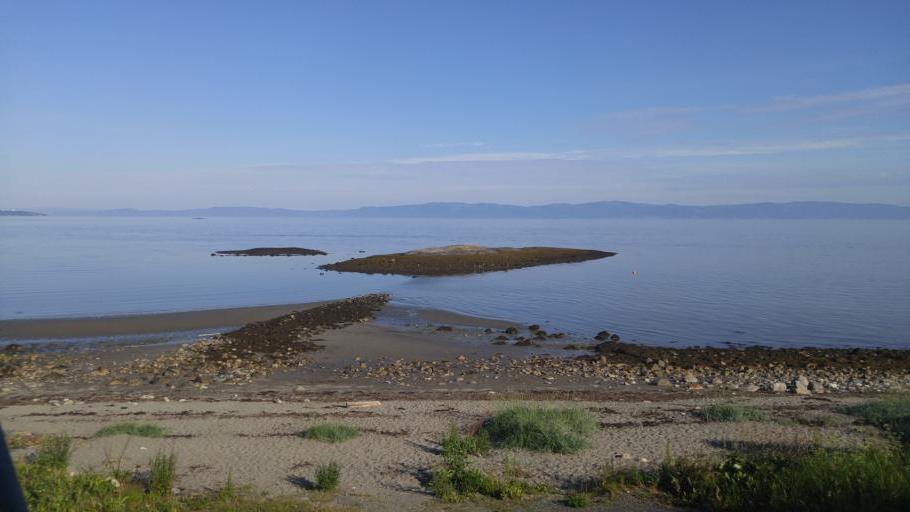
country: NO
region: Sor-Trondelag
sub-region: Malvik
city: Malvik
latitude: 63.4411
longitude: 10.6314
